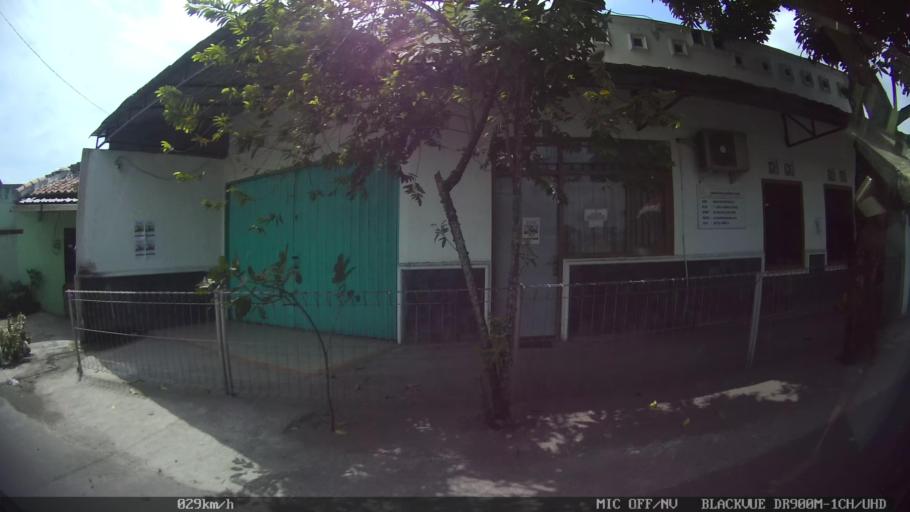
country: ID
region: Central Java
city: Candi Prambanan
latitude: -7.7830
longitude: 110.4782
